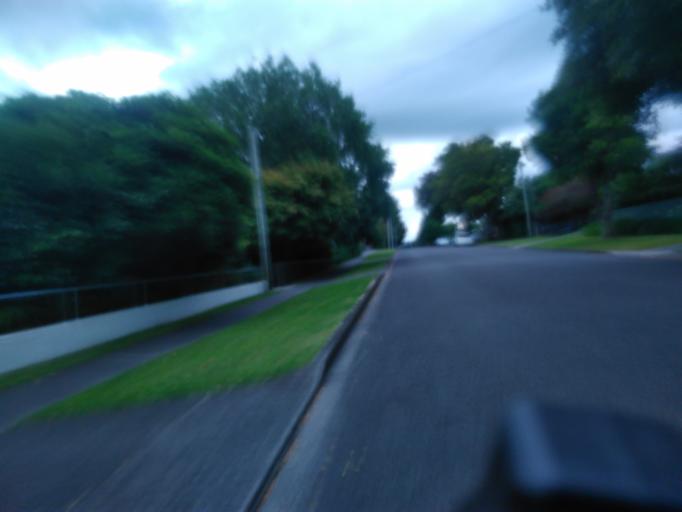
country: NZ
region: Gisborne
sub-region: Gisborne District
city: Gisborne
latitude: -38.6567
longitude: 178.0249
